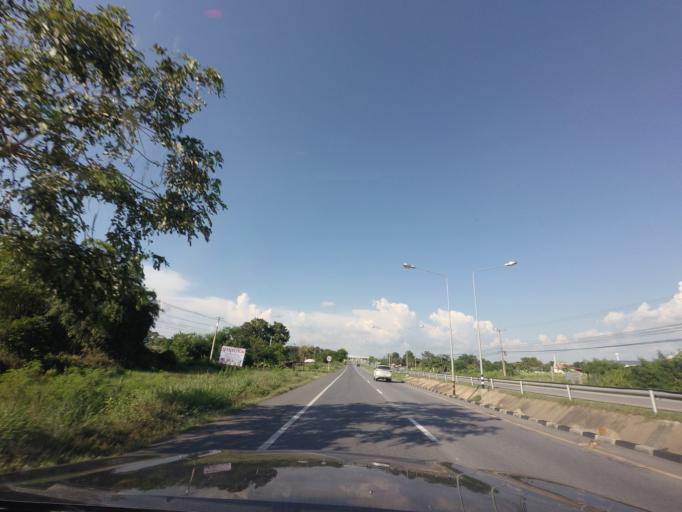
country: TH
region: Khon Kaen
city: Non Sila
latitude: 15.9479
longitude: 102.6813
